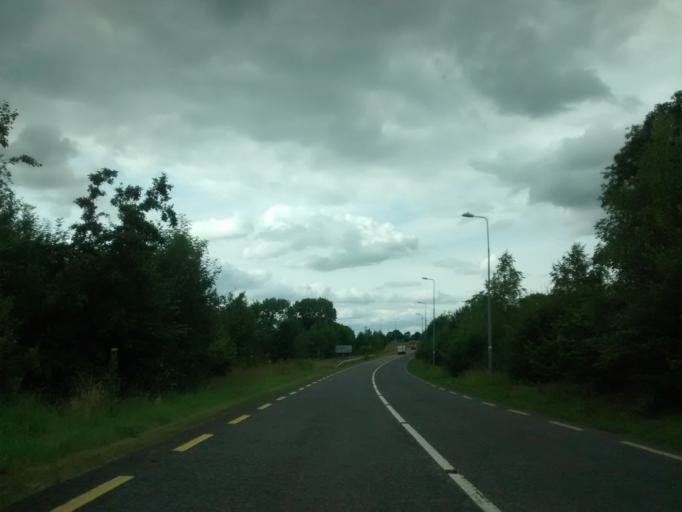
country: IE
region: Leinster
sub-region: An Iarmhi
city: Moate
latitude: 53.3933
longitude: -7.6877
